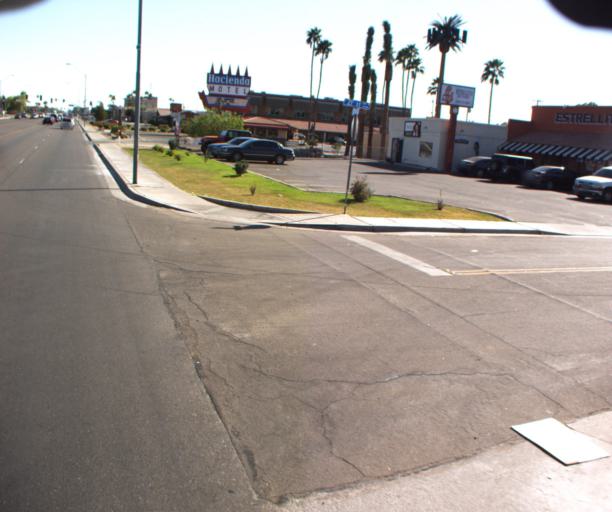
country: US
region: Arizona
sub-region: Yuma County
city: Yuma
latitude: 32.6895
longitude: -114.6247
